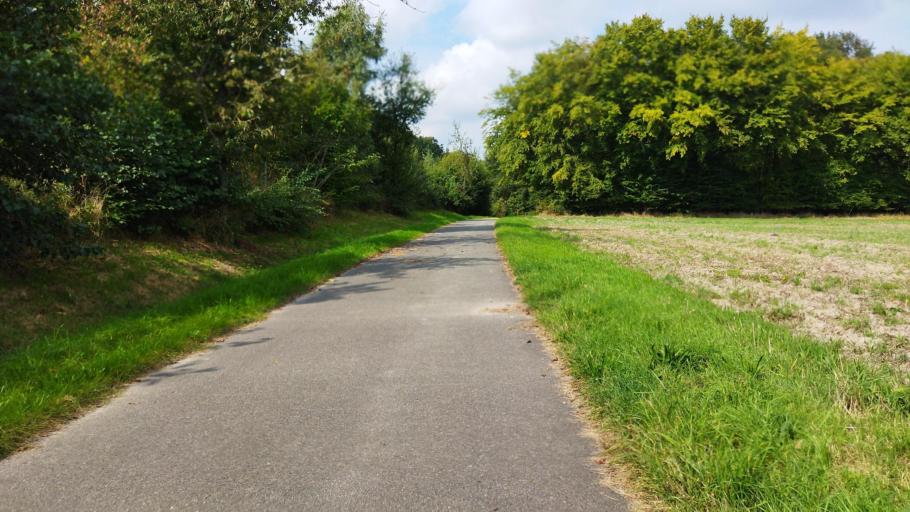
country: DE
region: North Rhine-Westphalia
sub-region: Regierungsbezirk Munster
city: Telgte
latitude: 51.9703
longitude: 7.8264
